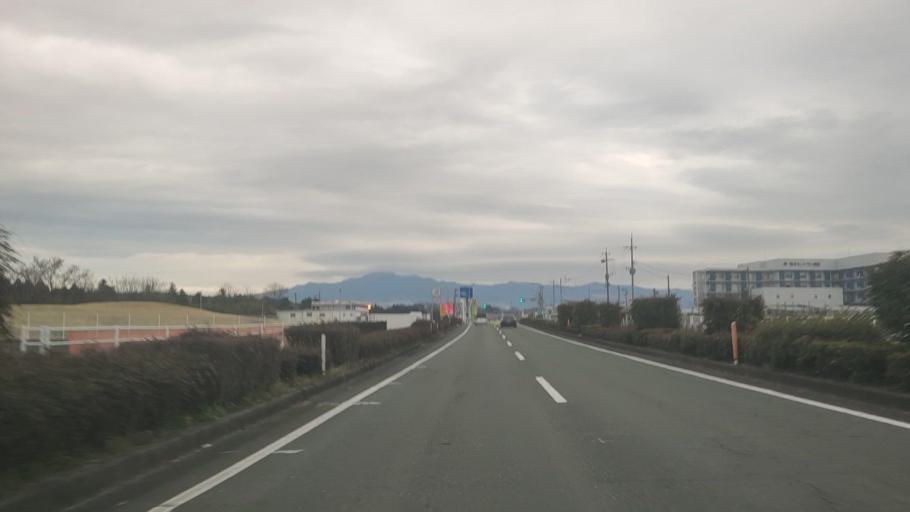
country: JP
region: Kumamoto
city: Ozu
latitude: 32.8725
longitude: 130.8460
